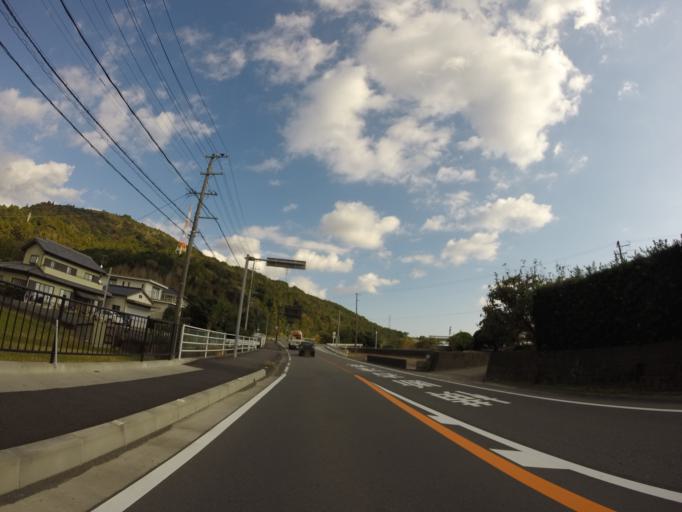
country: JP
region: Shizuoka
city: Kanaya
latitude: 34.8613
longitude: 138.1300
